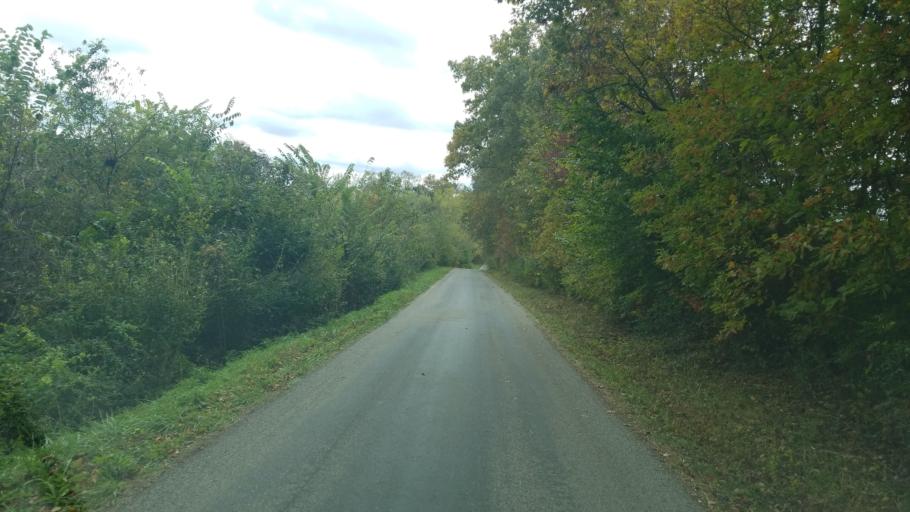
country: US
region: Ohio
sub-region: Jackson County
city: Wellston
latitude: 39.1638
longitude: -82.5667
